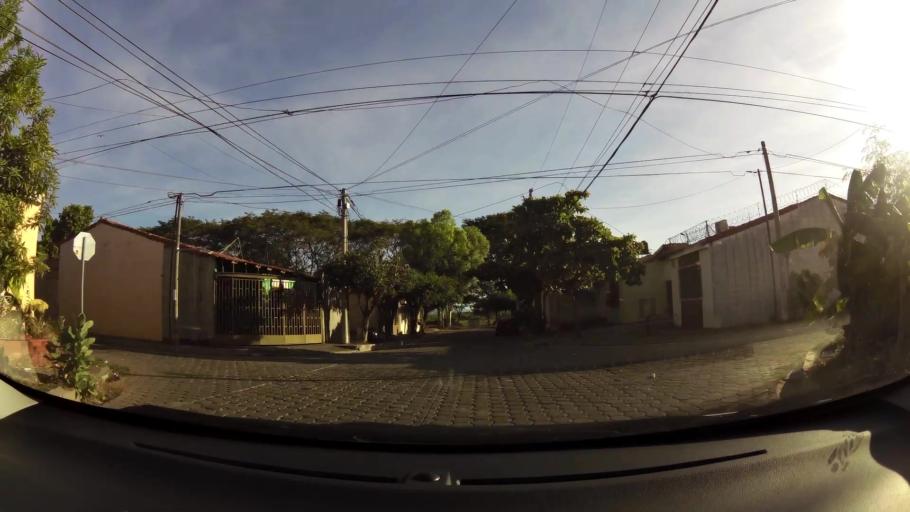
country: SV
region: San Miguel
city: San Miguel
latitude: 13.4563
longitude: -88.1670
